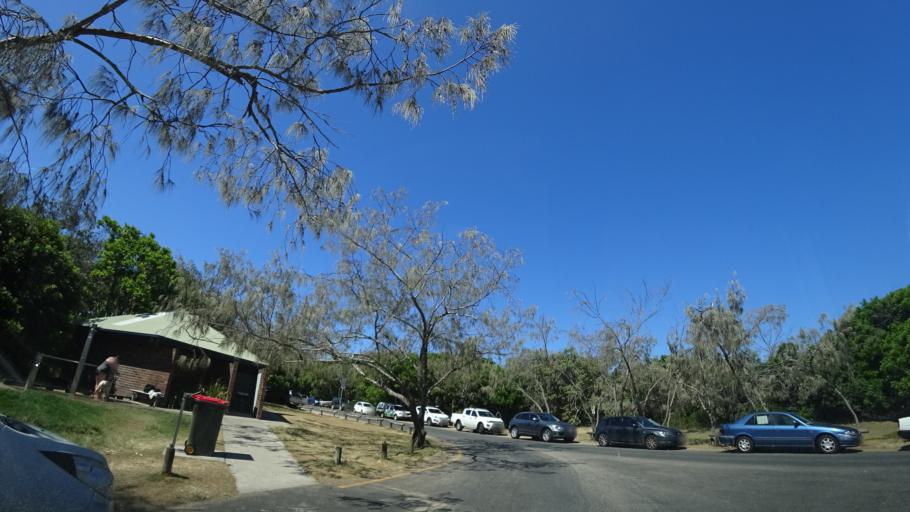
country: AU
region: Queensland
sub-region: Sunshine Coast
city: Mooloolaba
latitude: -26.6389
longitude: 153.1008
